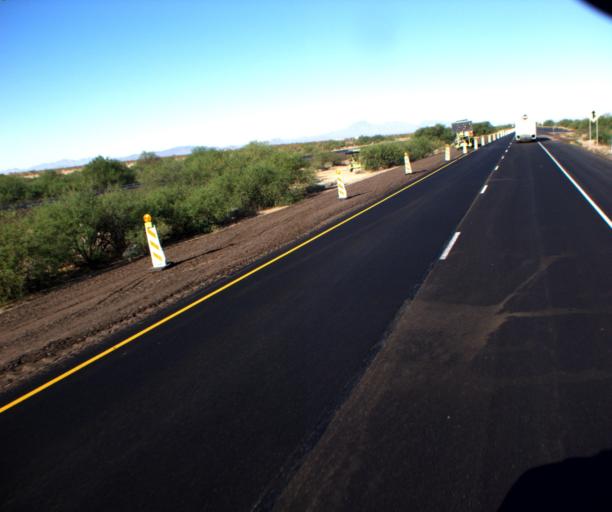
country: US
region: Arizona
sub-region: Pinal County
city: Casa Grande
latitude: 32.8282
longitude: -111.7770
